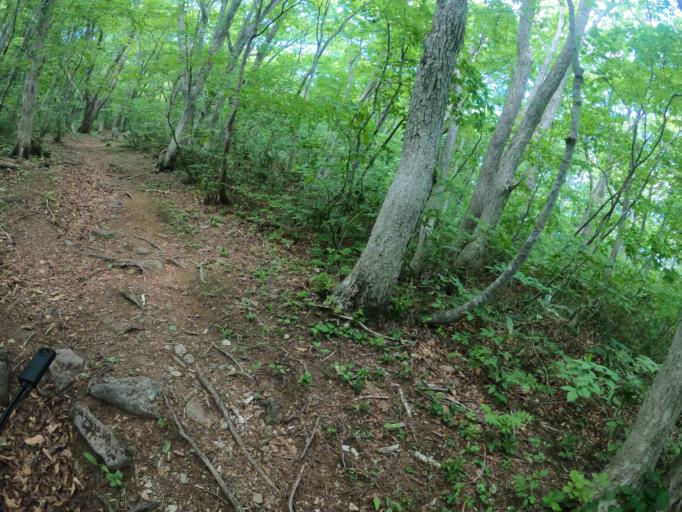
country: JP
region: Iwate
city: Ichinoseki
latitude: 38.9251
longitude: 140.7956
